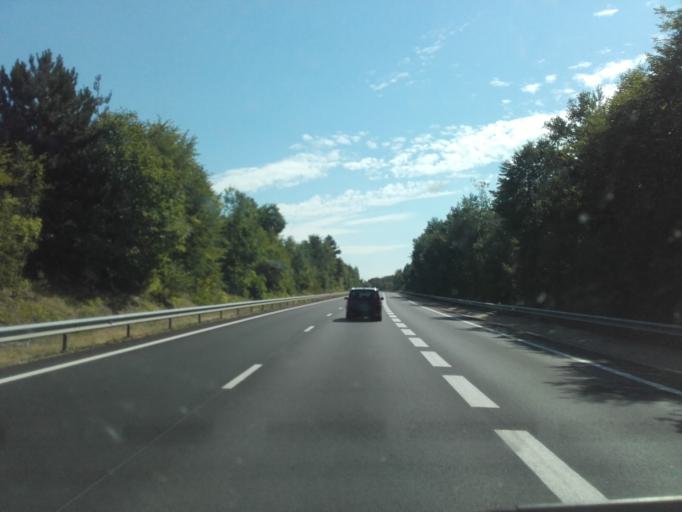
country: FR
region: Bourgogne
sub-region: Departement de la Cote-d'Or
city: Savigny-les-Beaune
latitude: 47.1391
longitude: 4.7009
